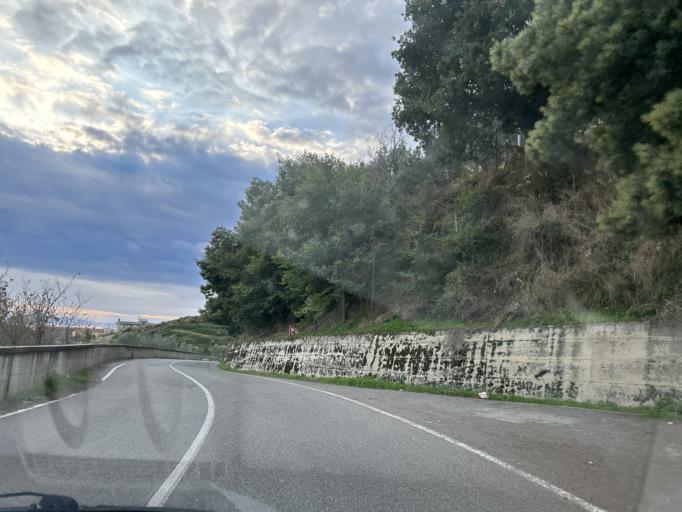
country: IT
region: Calabria
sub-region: Provincia di Catanzaro
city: Montauro
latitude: 38.7516
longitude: 16.5072
